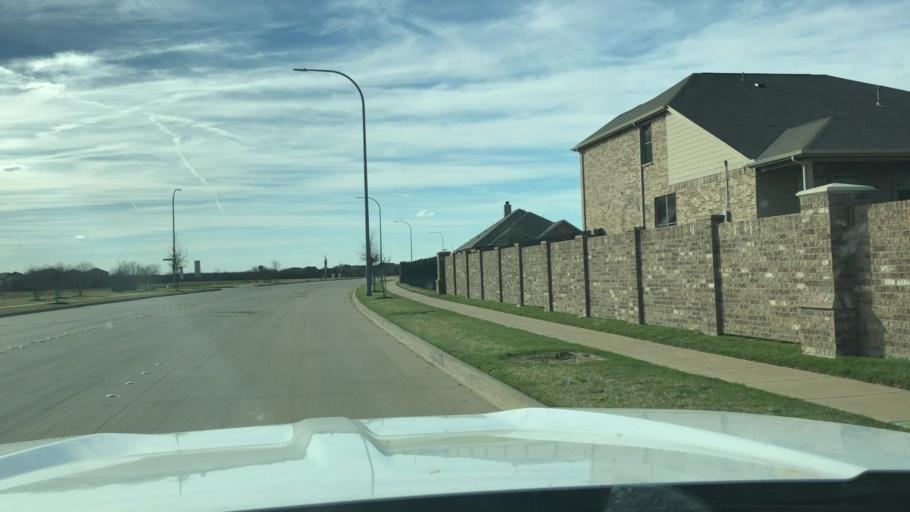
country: US
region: Texas
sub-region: Tarrant County
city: Haslet
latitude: 32.9892
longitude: -97.3676
